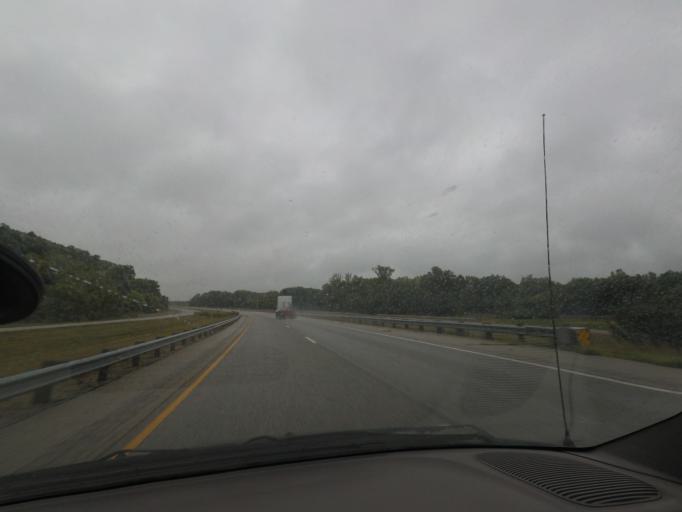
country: US
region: Illinois
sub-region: Pike County
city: Barry
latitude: 39.7131
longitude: -91.1025
